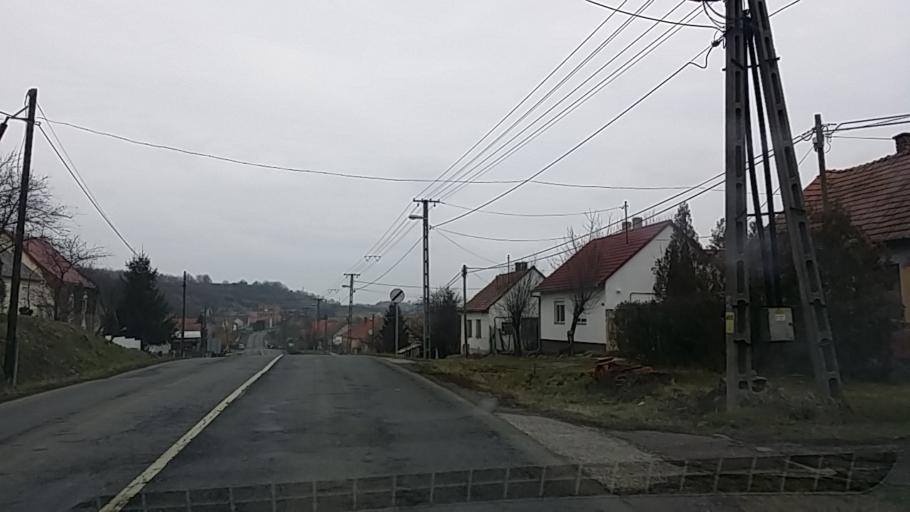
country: HU
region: Baranya
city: Dunaszekcso
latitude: 46.0723
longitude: 18.7535
